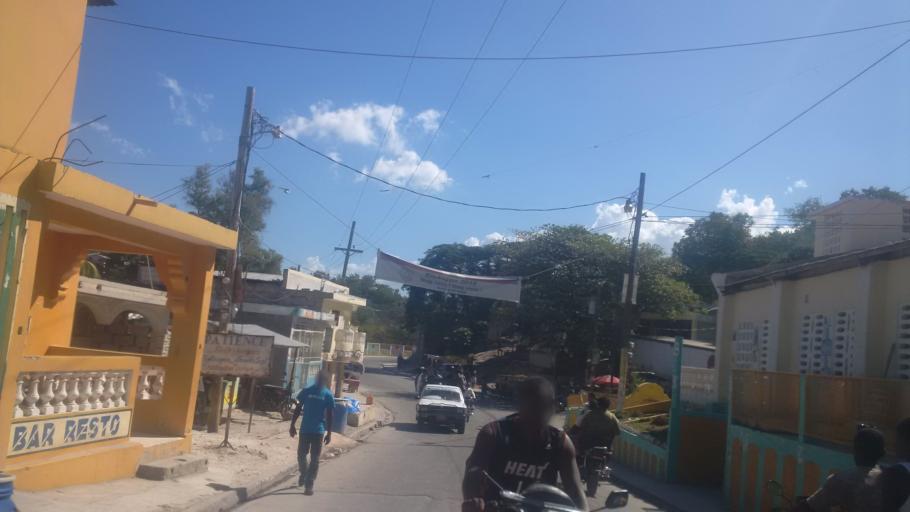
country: HT
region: Nippes
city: Miragoane
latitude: 18.4413
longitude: -73.0853
